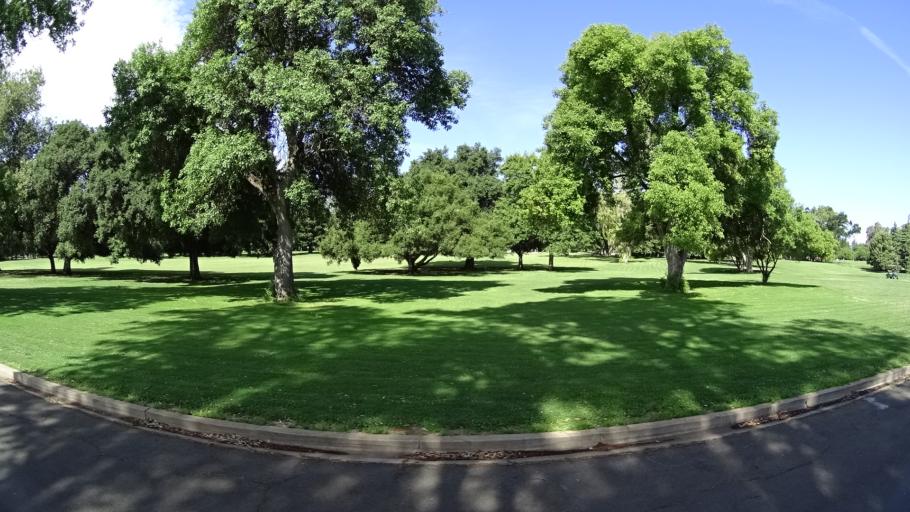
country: US
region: California
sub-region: Sacramento County
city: Sacramento
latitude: 38.5372
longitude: -121.4962
